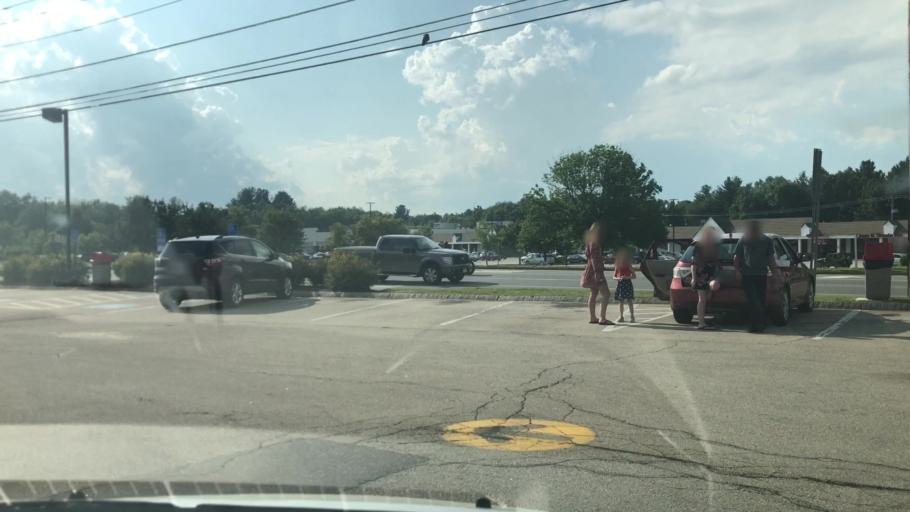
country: US
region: New Hampshire
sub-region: Hillsborough County
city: Milford
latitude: 42.8237
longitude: -71.6223
